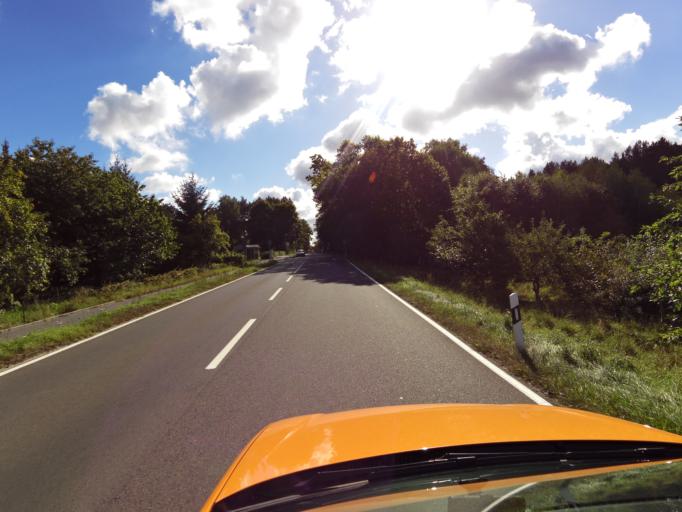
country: DE
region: Brandenburg
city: Michendorf
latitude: 52.2954
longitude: 13.0461
